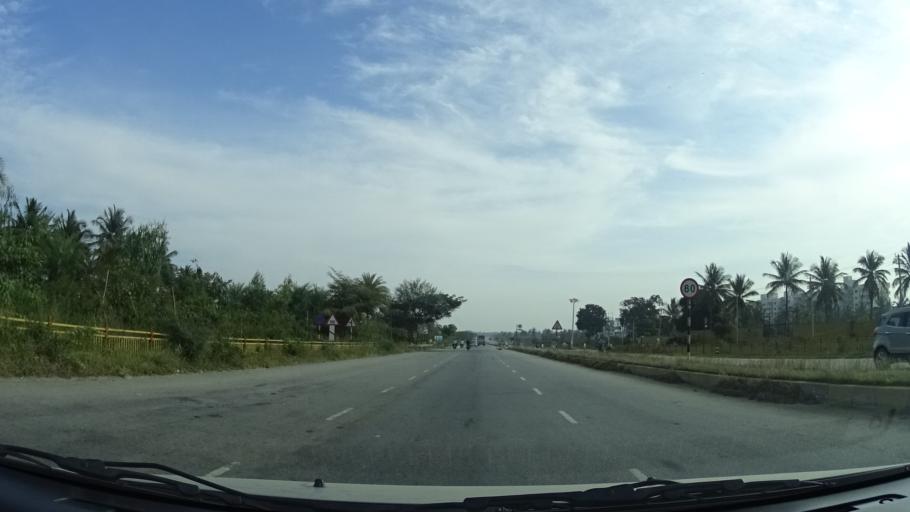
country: IN
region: Karnataka
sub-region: Bangalore Rural
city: Devanhalli
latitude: 13.2295
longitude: 77.6902
